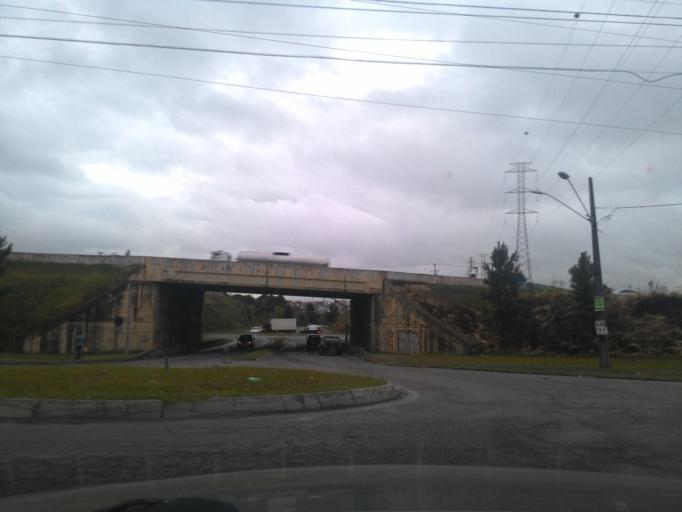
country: BR
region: Parana
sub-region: Araucaria
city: Araucaria
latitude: -25.5517
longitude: -49.3336
